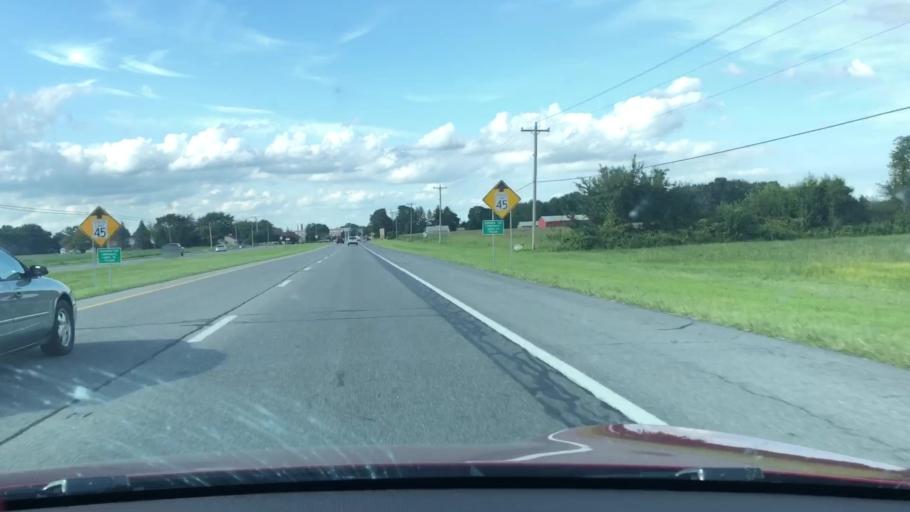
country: US
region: Delaware
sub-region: Kent County
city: Felton
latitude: 39.0006
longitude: -75.5686
